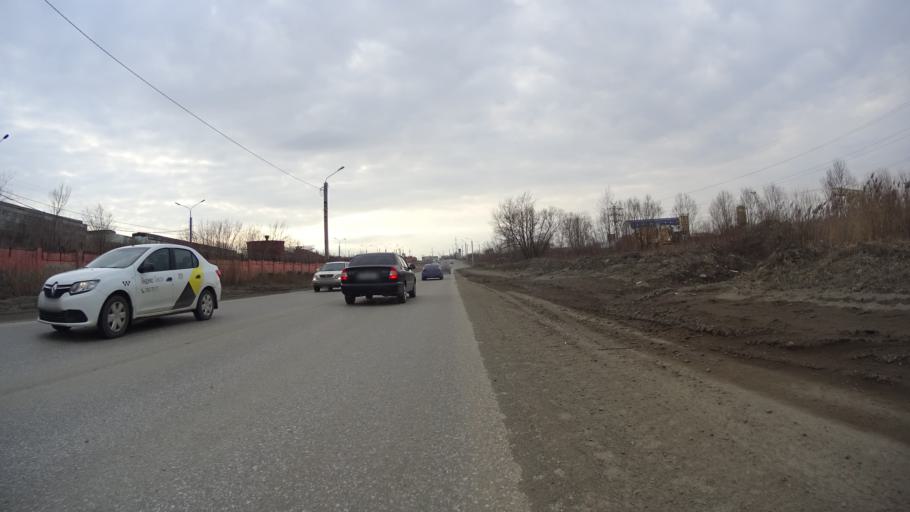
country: RU
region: Chelyabinsk
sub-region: Gorod Chelyabinsk
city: Chelyabinsk
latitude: 55.1573
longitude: 61.4909
